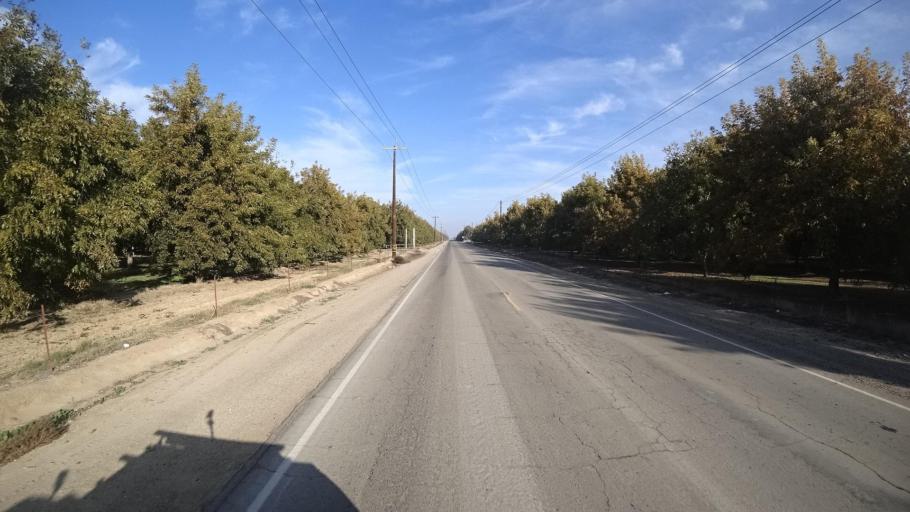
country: US
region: California
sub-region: Kern County
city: McFarland
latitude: 35.6196
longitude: -119.2044
